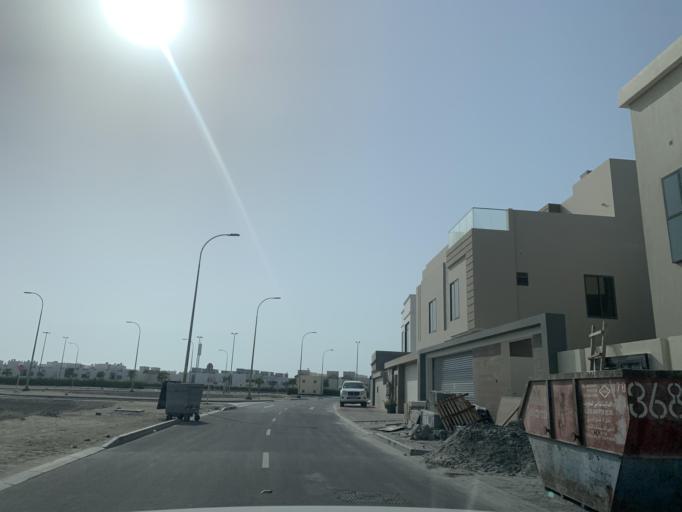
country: BH
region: Muharraq
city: Al Muharraq
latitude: 26.3118
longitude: 50.6342
